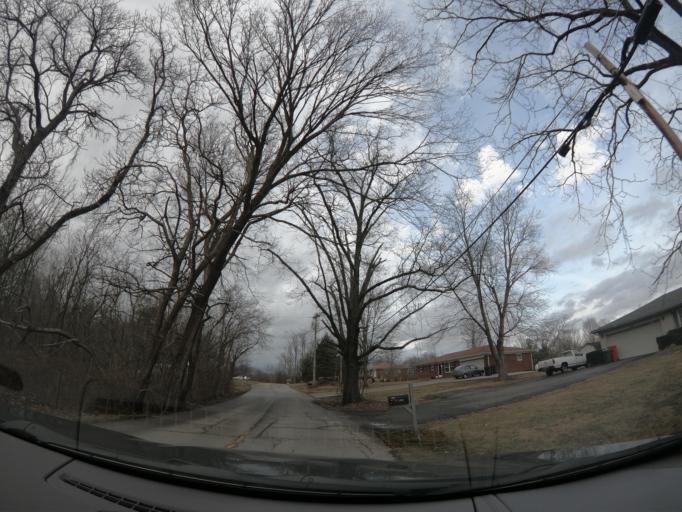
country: US
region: Indiana
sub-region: Floyd County
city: Galena
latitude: 38.3503
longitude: -85.9173
